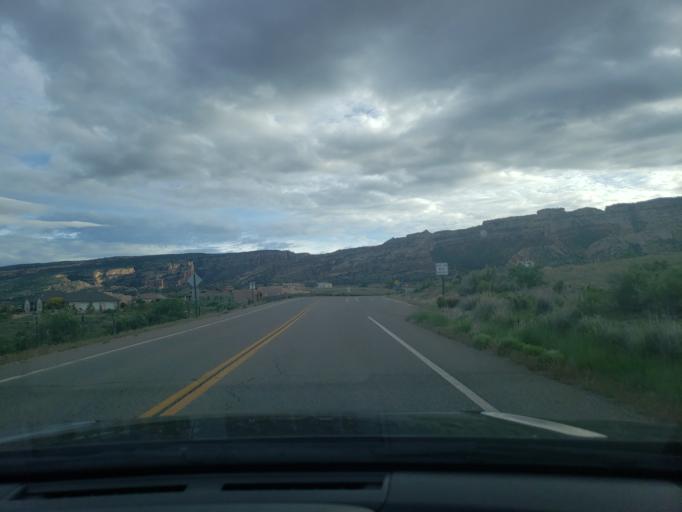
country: US
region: Colorado
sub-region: Mesa County
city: Redlands
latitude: 39.0441
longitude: -108.6245
